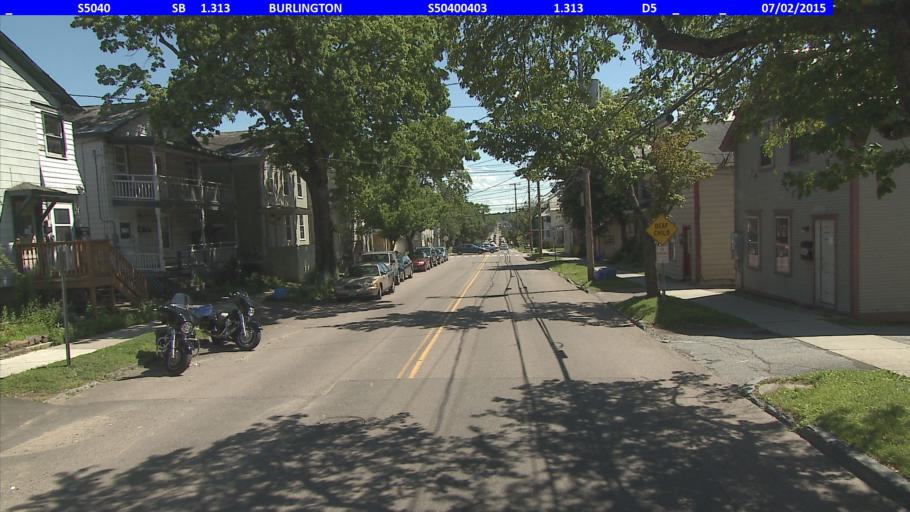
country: US
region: Vermont
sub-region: Chittenden County
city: Burlington
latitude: 44.4743
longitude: -73.2155
